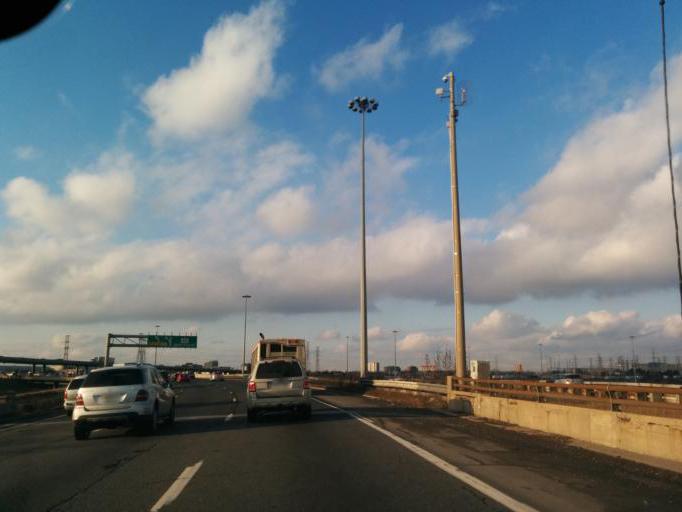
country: CA
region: Ontario
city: Etobicoke
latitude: 43.6712
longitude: -79.5747
